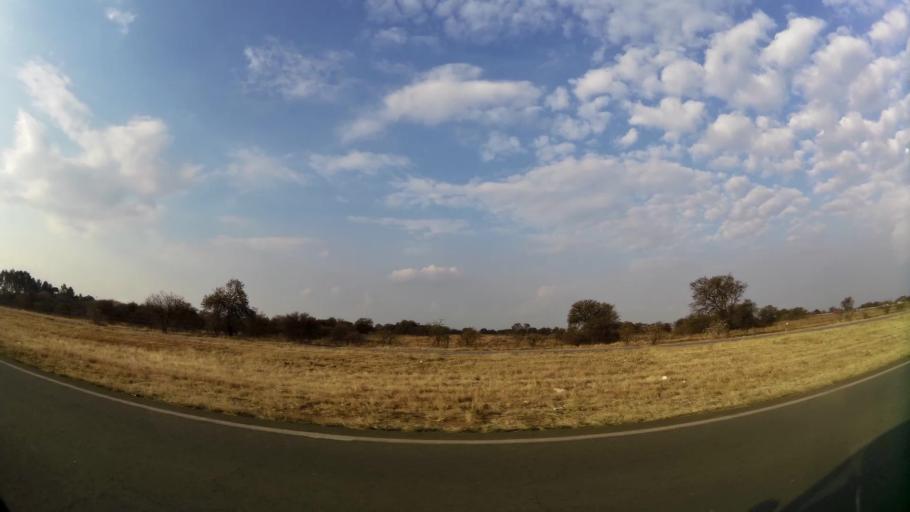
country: ZA
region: Gauteng
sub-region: Sedibeng District Municipality
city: Vereeniging
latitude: -26.6329
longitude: 27.8689
